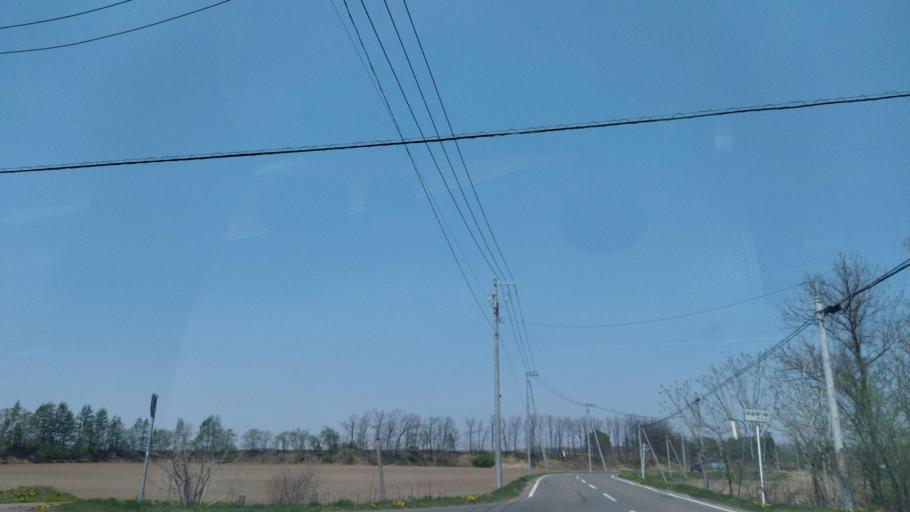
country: JP
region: Hokkaido
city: Obihiro
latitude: 42.8942
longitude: 143.0295
